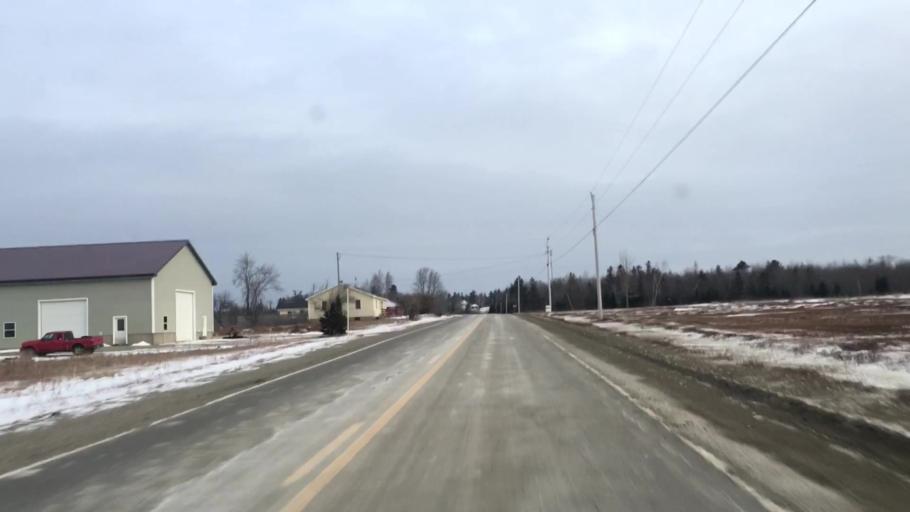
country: US
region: Maine
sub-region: Hancock County
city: Franklin
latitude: 44.7183
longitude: -68.3360
